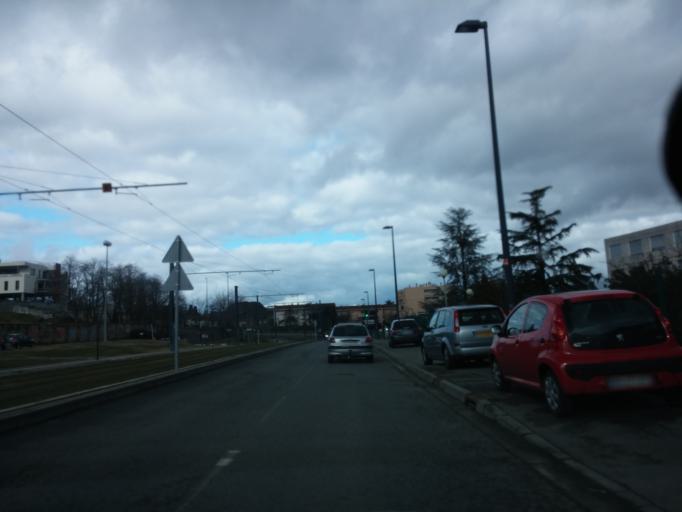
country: FR
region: Midi-Pyrenees
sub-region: Departement de la Haute-Garonne
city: Blagnac
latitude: 43.6119
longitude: 1.4015
